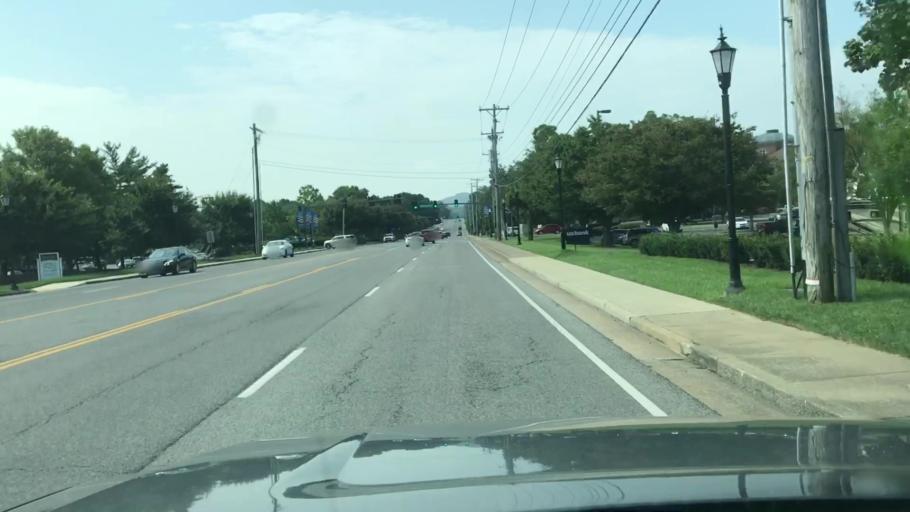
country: US
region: Tennessee
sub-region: Williamson County
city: Brentwood
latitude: 36.0296
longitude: -86.7909
